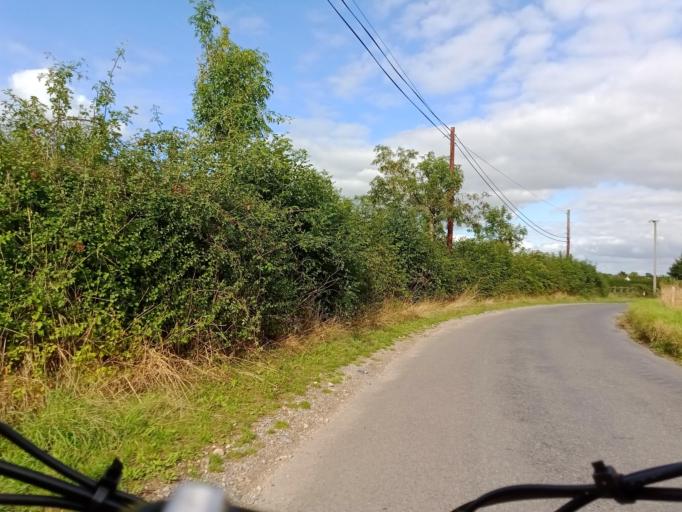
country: IE
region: Leinster
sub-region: Kilkenny
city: Kilkenny
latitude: 52.6068
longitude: -7.2243
